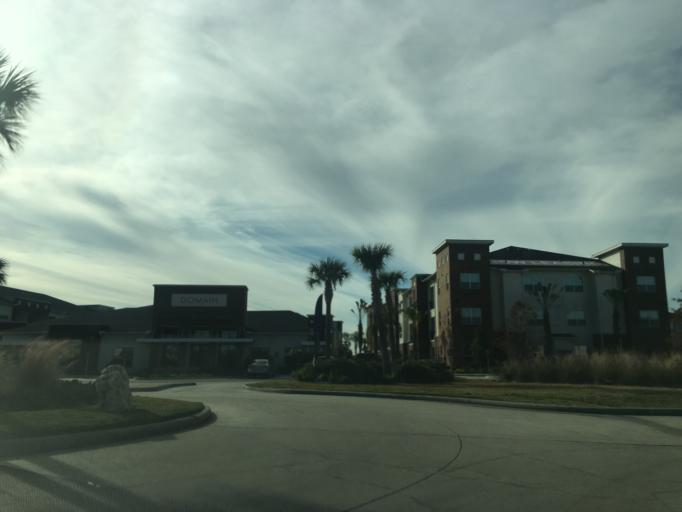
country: US
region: Texas
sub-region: Harris County
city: Cloverleaf
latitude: 29.8159
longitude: -95.1658
